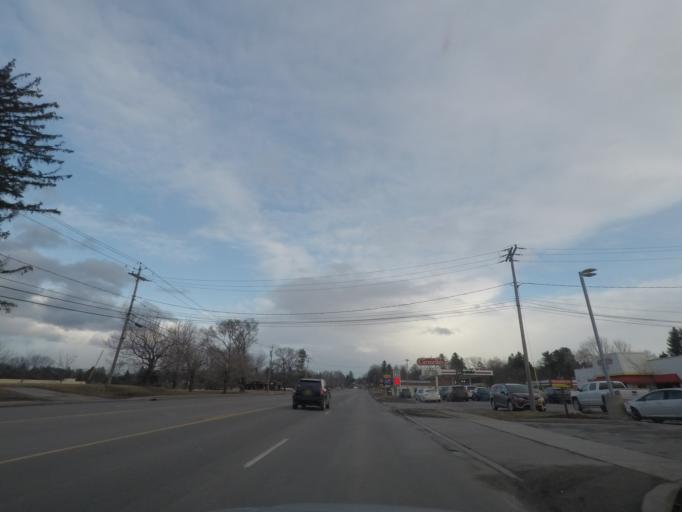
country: US
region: New York
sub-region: Oneida County
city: New Hartford
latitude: 43.0799
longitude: -75.3183
